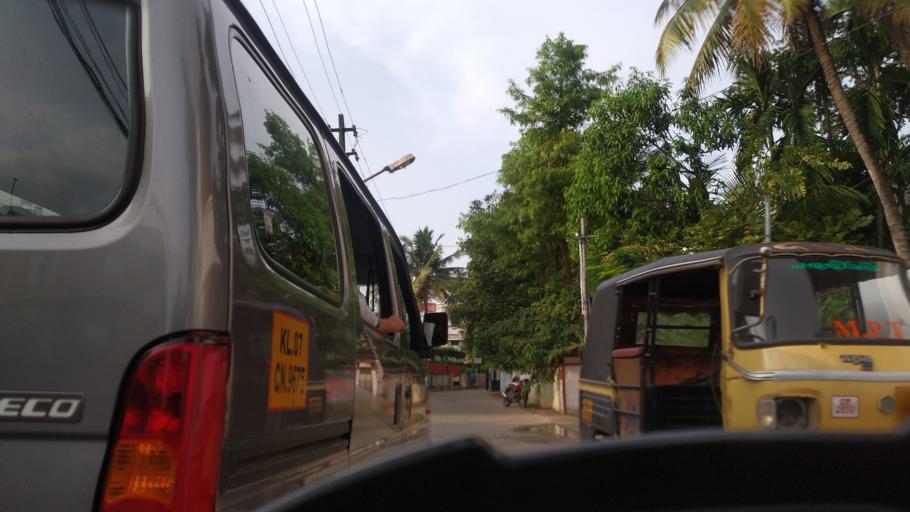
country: IN
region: Kerala
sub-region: Ernakulam
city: Cochin
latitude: 9.9841
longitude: 76.3091
